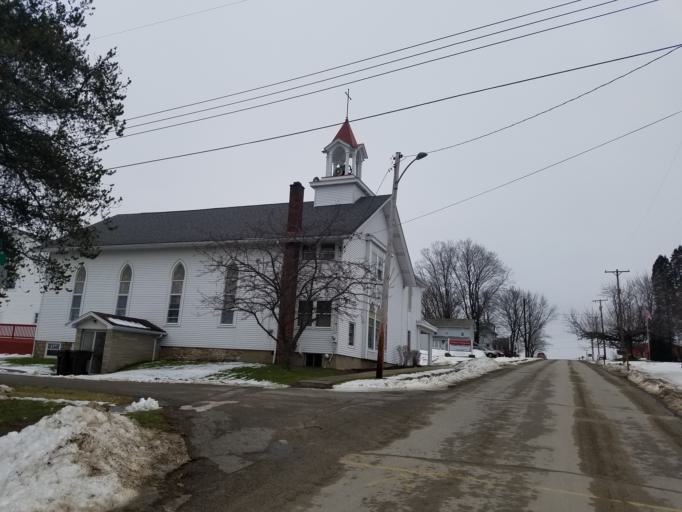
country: US
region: Pennsylvania
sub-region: Mercer County
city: Mercer
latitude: 41.3197
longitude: -80.2578
